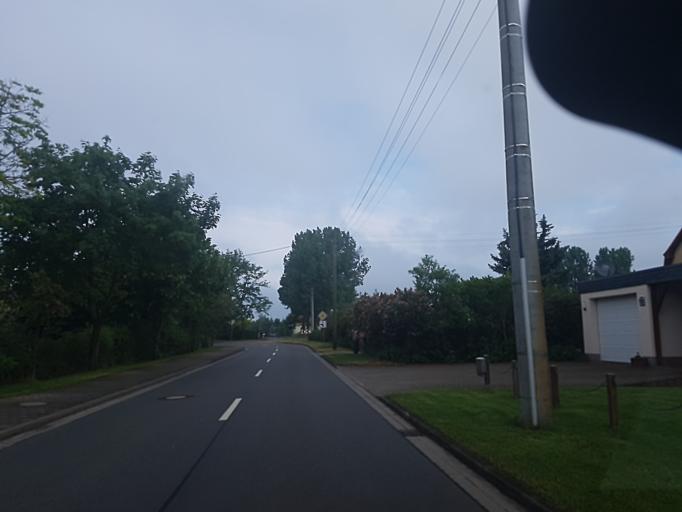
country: DE
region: Saxony-Anhalt
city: Klieken
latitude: 51.9679
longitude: 12.3401
